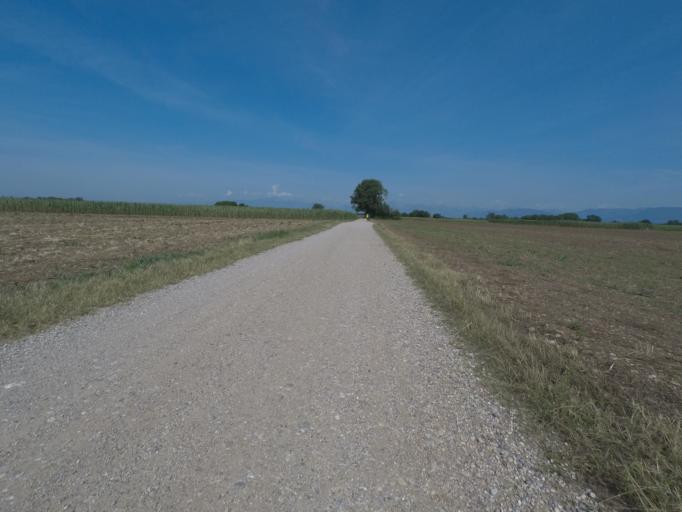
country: IT
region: Friuli Venezia Giulia
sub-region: Provincia di Udine
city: Mereto di Tomba
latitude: 46.0674
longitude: 13.0540
